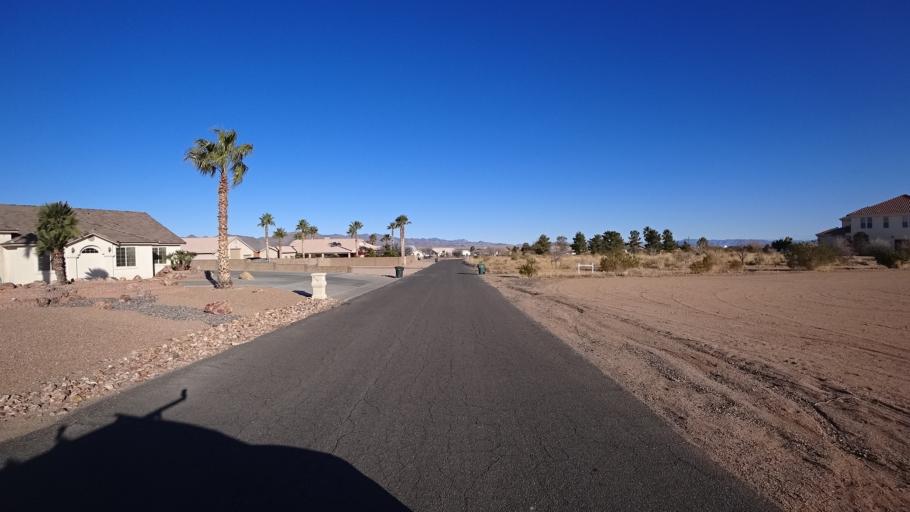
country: US
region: Arizona
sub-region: Mohave County
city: Kingman
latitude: 35.2054
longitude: -113.9955
